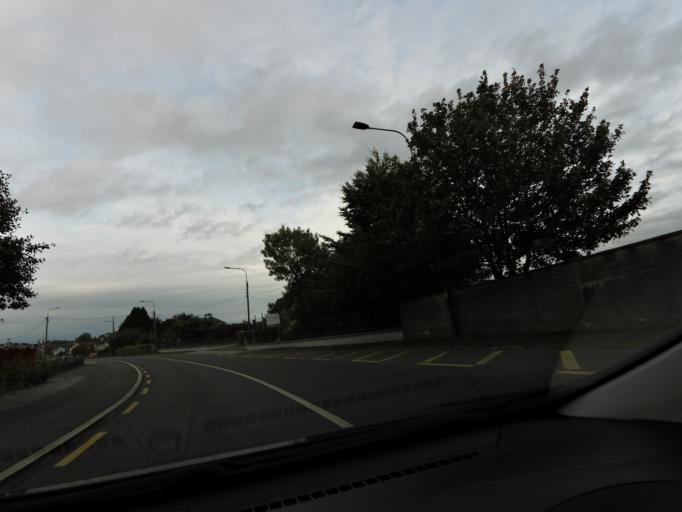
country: IE
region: Leinster
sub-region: Uibh Fhaili
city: Ferbane
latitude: 53.2662
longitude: -7.8291
